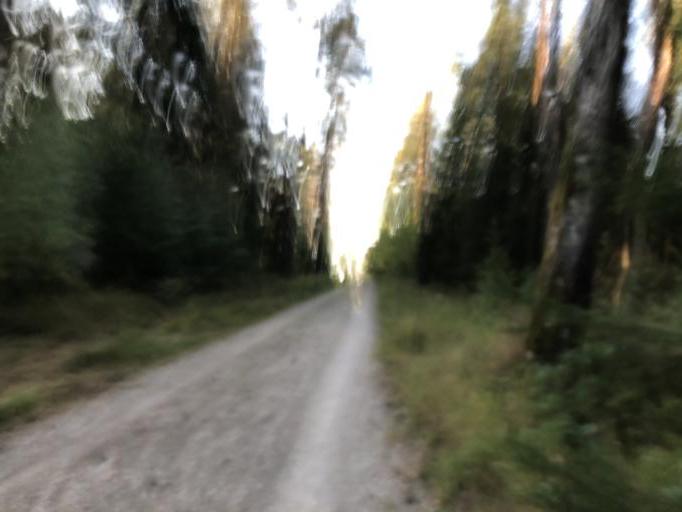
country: DE
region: Bavaria
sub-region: Regierungsbezirk Mittelfranken
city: Uttenreuth
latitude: 49.5772
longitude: 11.0738
